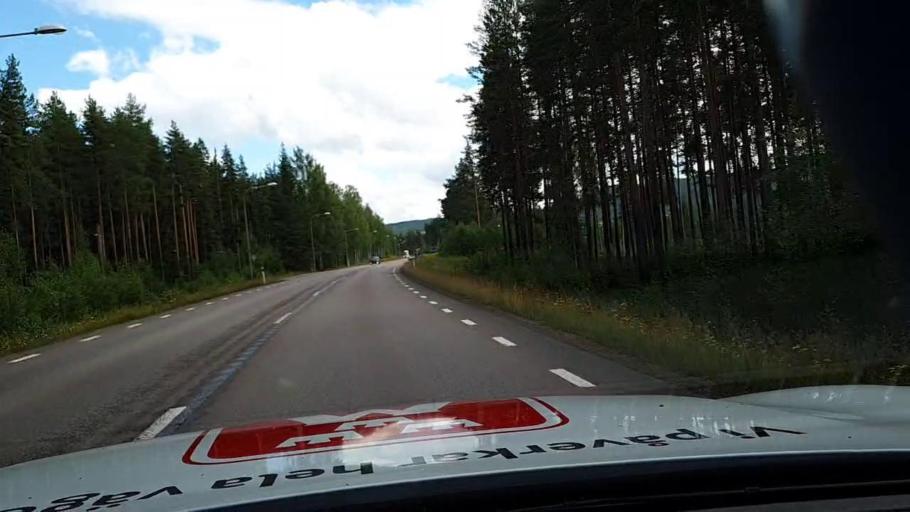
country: SE
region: Jaemtland
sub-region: Ragunda Kommun
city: Hammarstrand
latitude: 63.1474
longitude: 16.0843
